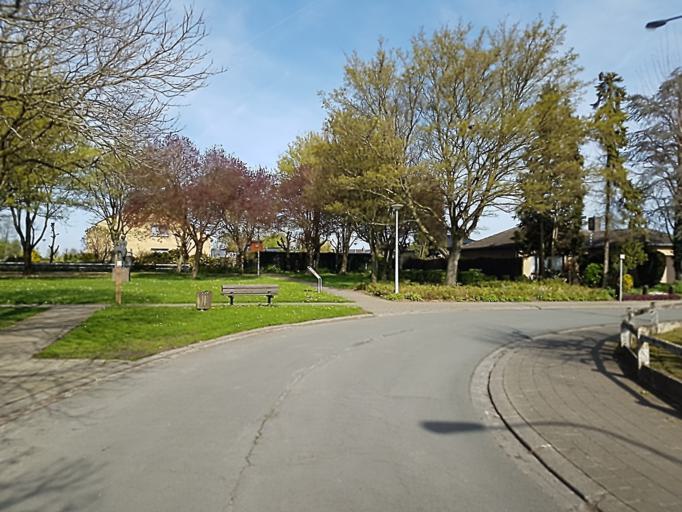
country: BE
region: Flanders
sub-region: Provincie West-Vlaanderen
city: Avelgem
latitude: 50.8198
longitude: 3.4311
